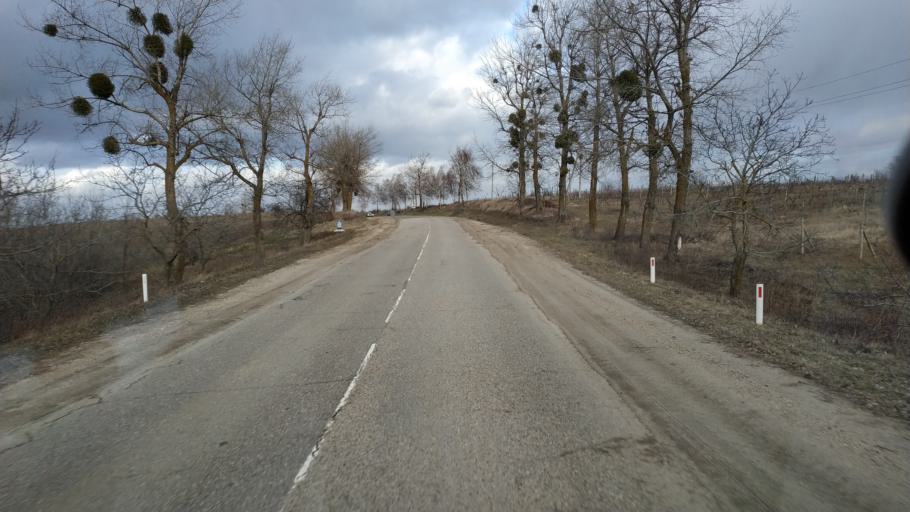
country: MD
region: Calarasi
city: Calarasi
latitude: 47.2875
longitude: 28.3554
